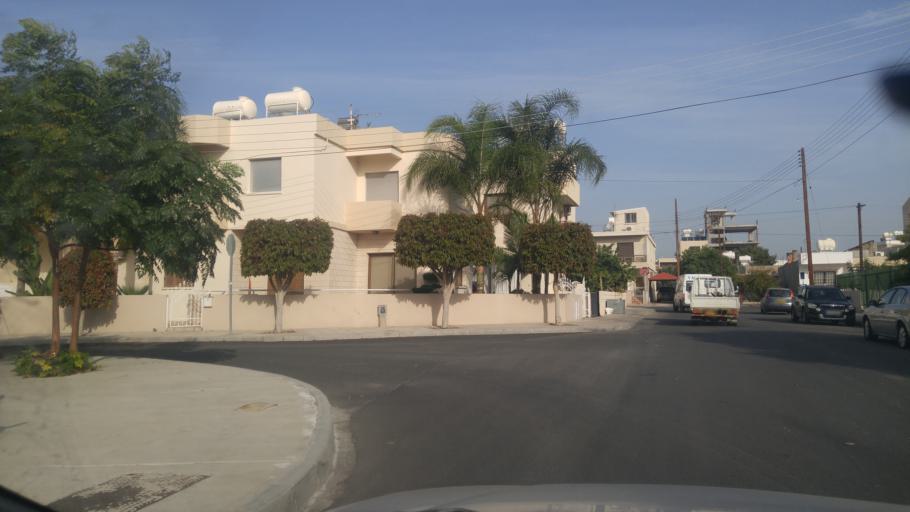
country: CY
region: Limassol
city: Limassol
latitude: 34.6633
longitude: 33.0068
